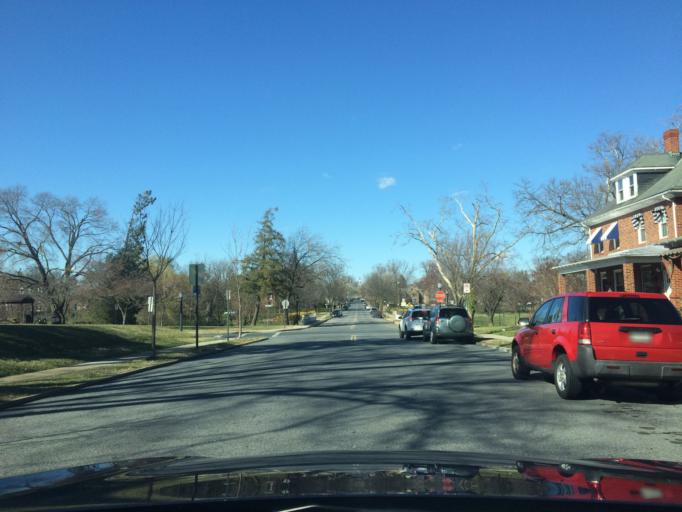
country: US
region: Maryland
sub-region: Frederick County
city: Frederick
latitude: 39.4145
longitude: -77.4184
